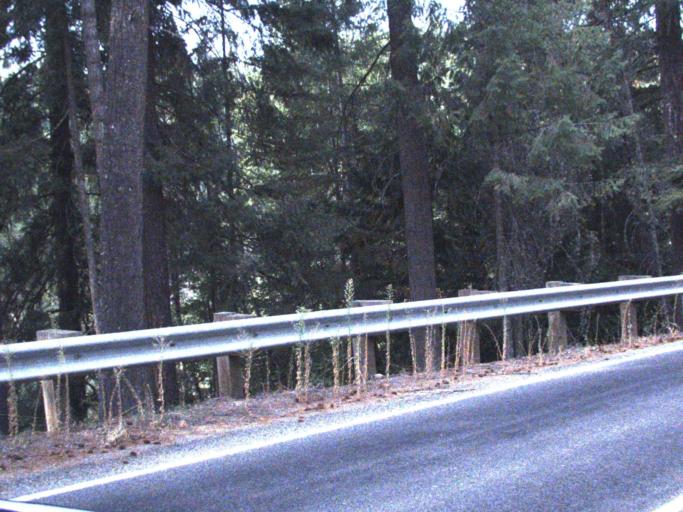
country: US
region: Washington
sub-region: Spokane County
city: Trentwood
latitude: 47.8346
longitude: -117.1992
